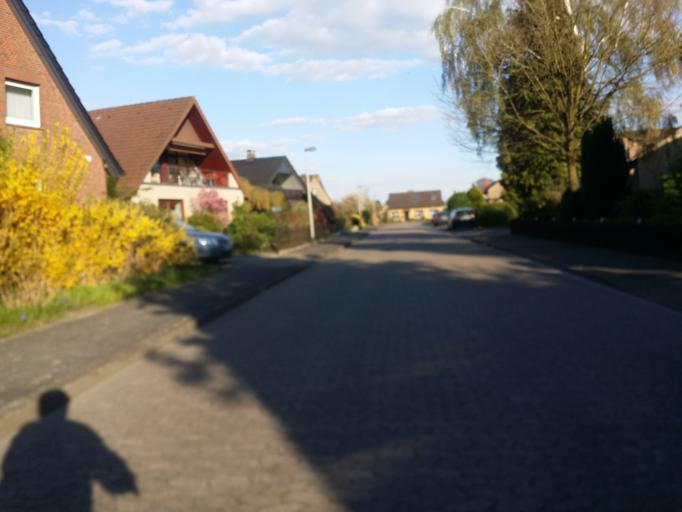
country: DE
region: Lower Saxony
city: Delmenhorst
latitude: 53.0230
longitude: 8.6236
